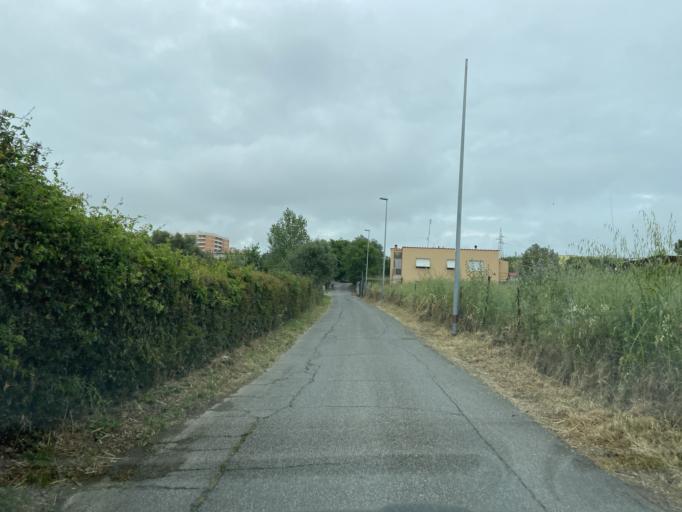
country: IT
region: Latium
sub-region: Citta metropolitana di Roma Capitale
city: Civitavecchia
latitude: 42.0902
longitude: 11.8131
